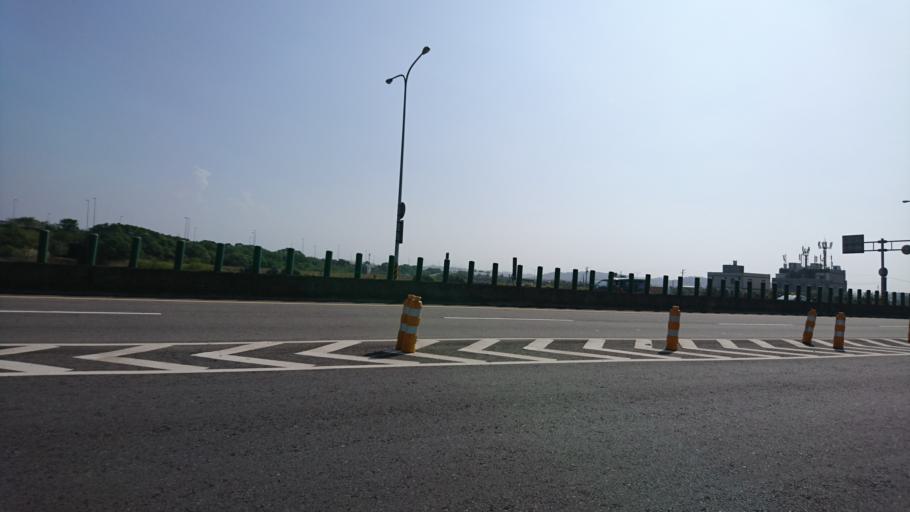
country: TW
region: Taiwan
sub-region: Miaoli
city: Miaoli
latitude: 24.6794
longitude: 120.8453
